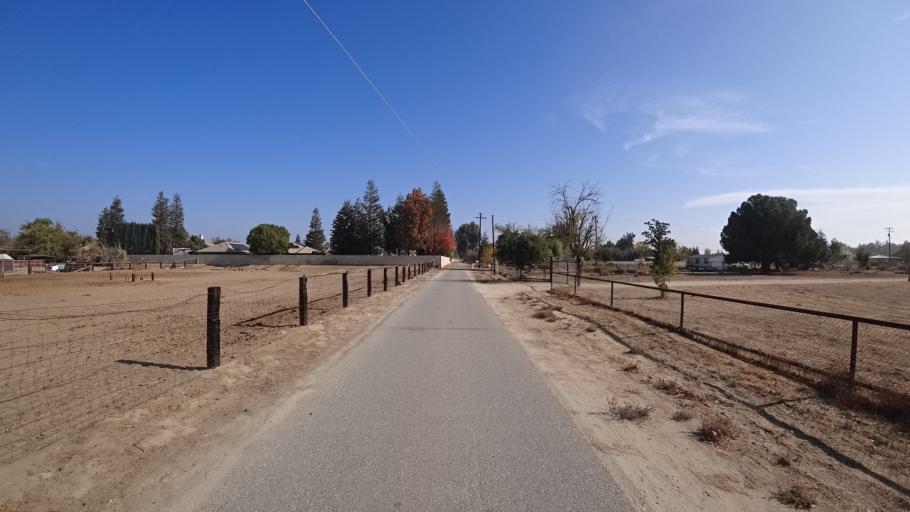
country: US
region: California
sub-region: Kern County
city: Rosedale
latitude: 35.3653
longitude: -119.1596
